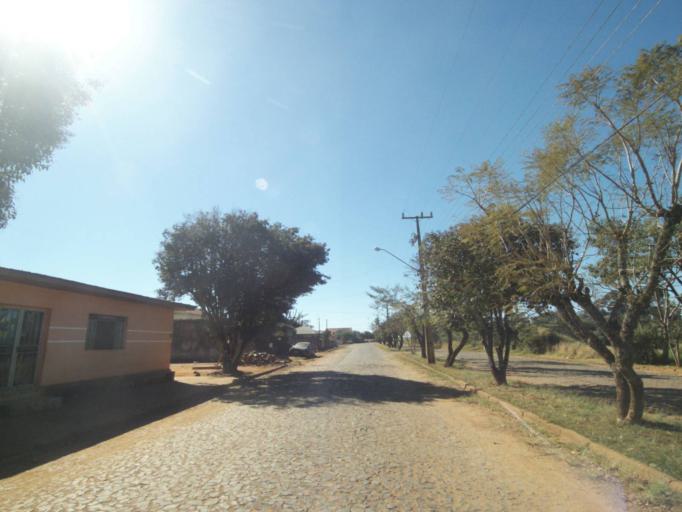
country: BR
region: Parana
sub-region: Reserva
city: Reserva
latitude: -24.6222
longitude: -50.6393
